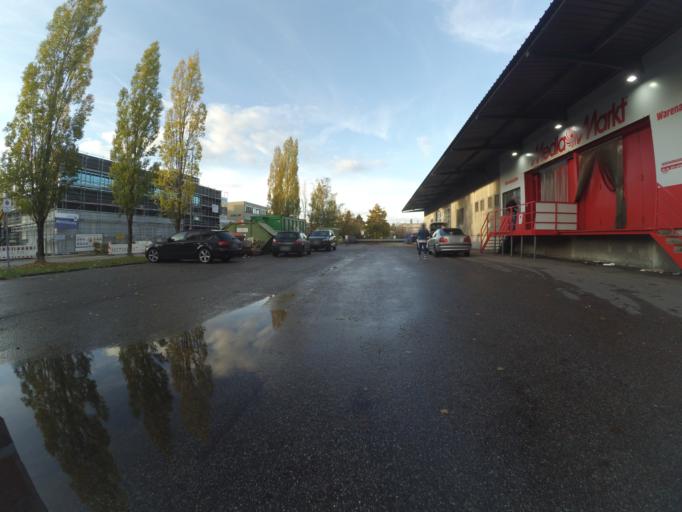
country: DE
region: Bavaria
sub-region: Upper Bavaria
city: Bogenhausen
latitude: 48.1937
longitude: 11.5905
